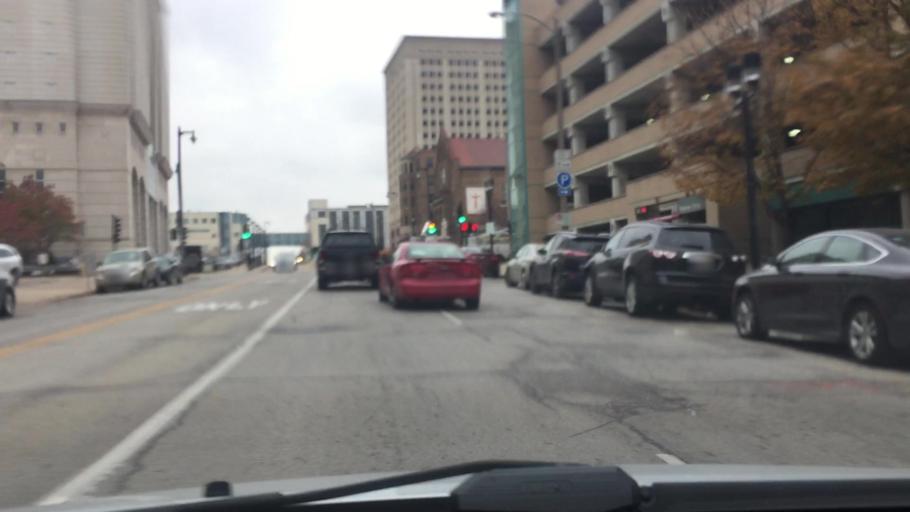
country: US
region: Wisconsin
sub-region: Milwaukee County
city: Milwaukee
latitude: 43.0431
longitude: -87.9221
